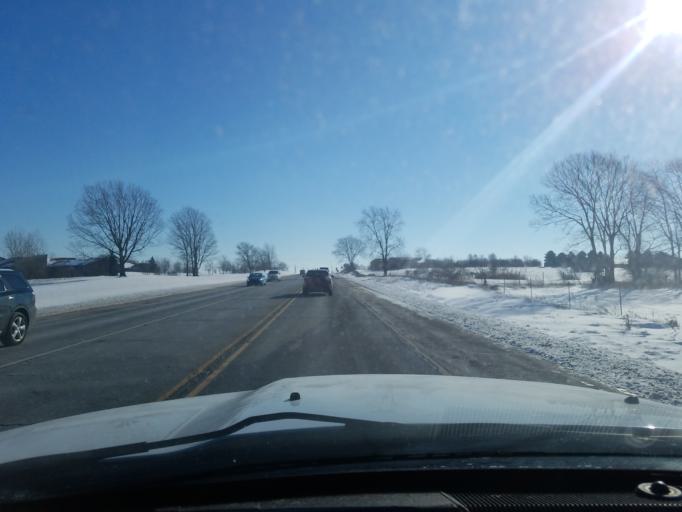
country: US
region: Indiana
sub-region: Noble County
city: Kendallville
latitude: 41.4476
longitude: -85.2368
